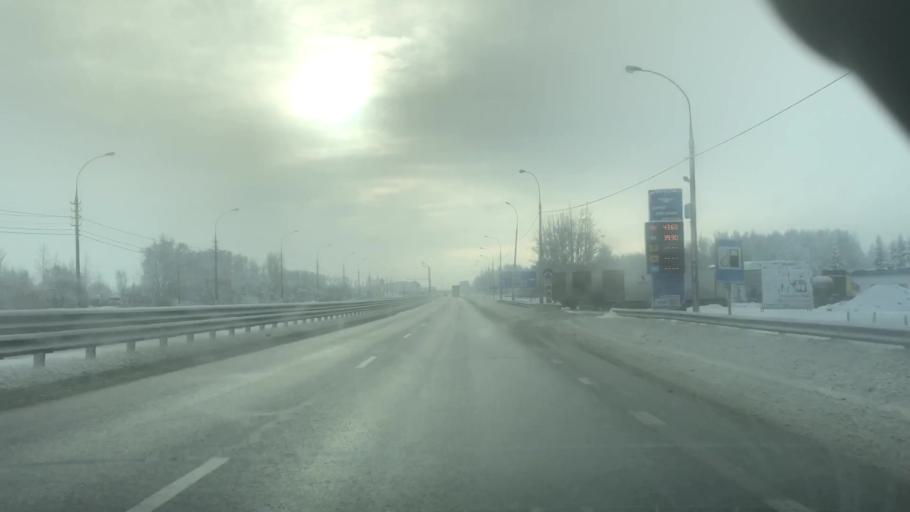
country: RU
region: Tula
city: Venev
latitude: 54.3427
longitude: 38.1545
